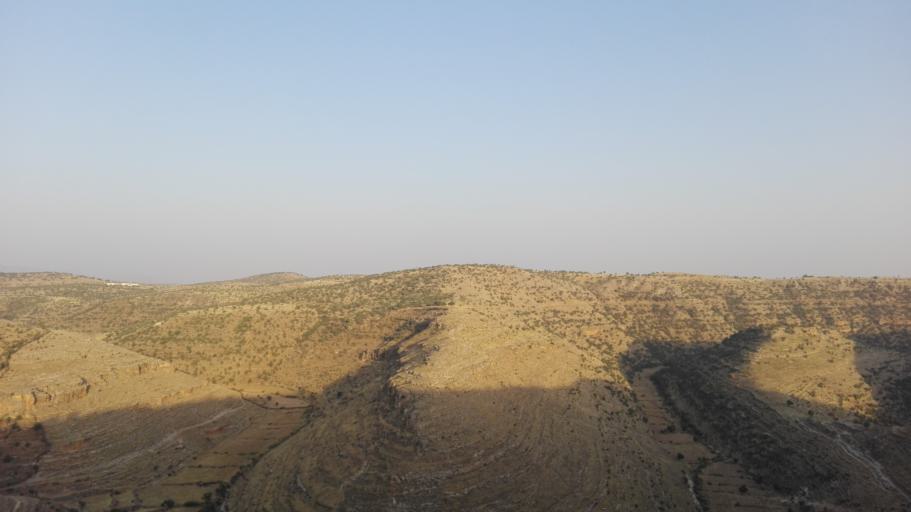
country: TR
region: Mardin
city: Kilavuz
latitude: 37.4748
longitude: 41.7871
